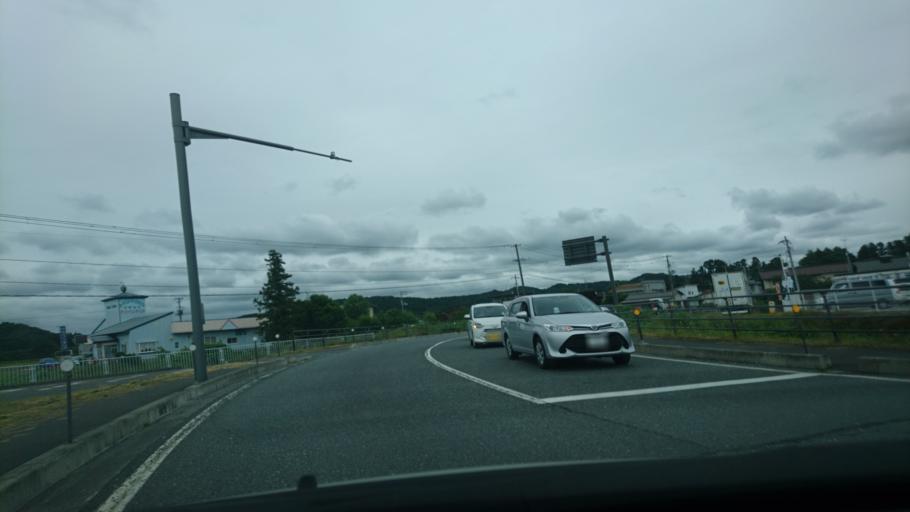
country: JP
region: Iwate
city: Ichinoseki
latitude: 38.9735
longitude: 141.1180
